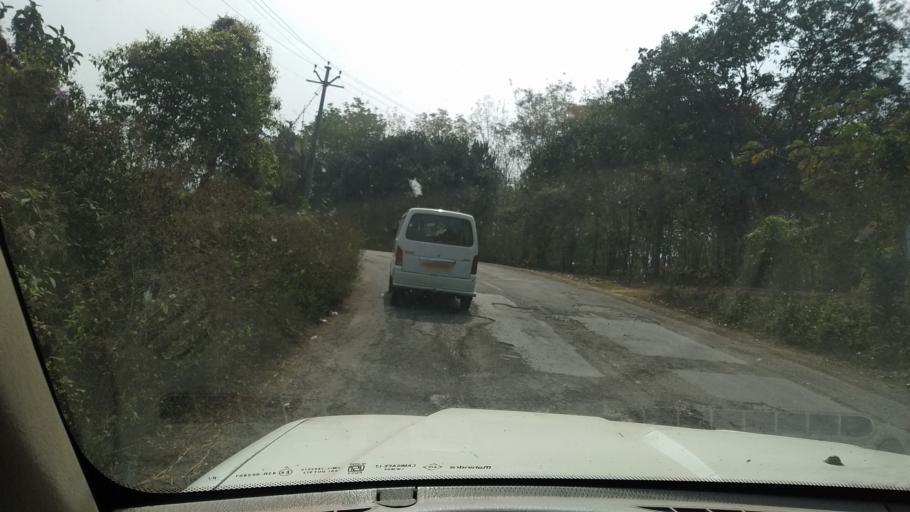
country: BD
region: Chittagong
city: Comilla
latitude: 23.5985
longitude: 91.1793
